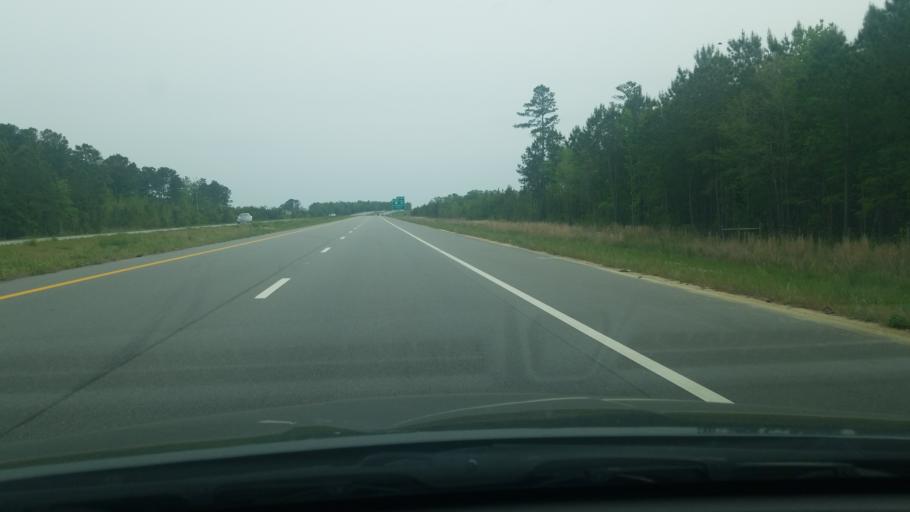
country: US
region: North Carolina
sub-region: Jones County
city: Maysville
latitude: 34.9904
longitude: -77.2357
